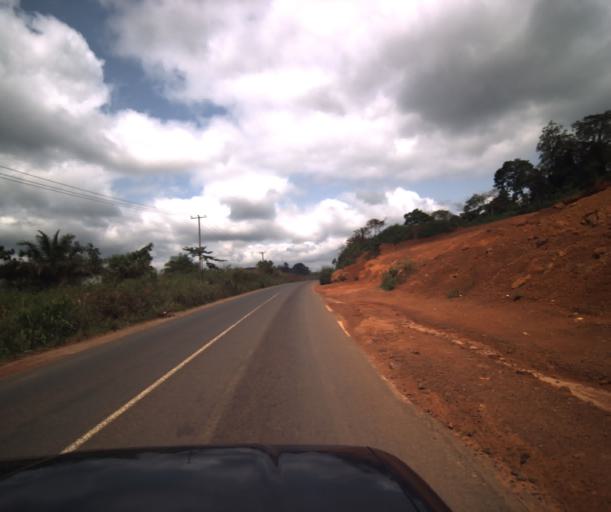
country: CM
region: Centre
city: Mbankomo
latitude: 3.7856
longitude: 11.4497
